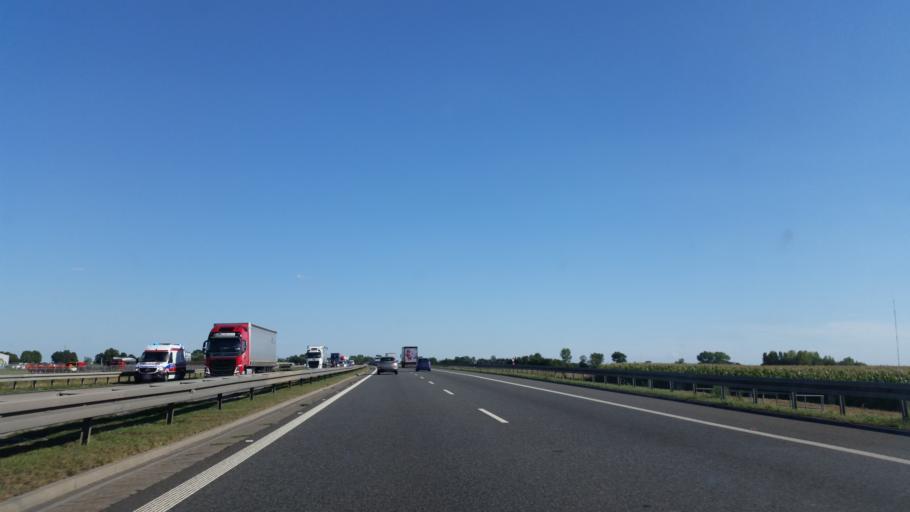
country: PL
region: Lower Silesian Voivodeship
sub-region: Powiat wroclawski
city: Zorawina
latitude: 51.0108
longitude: 17.0282
